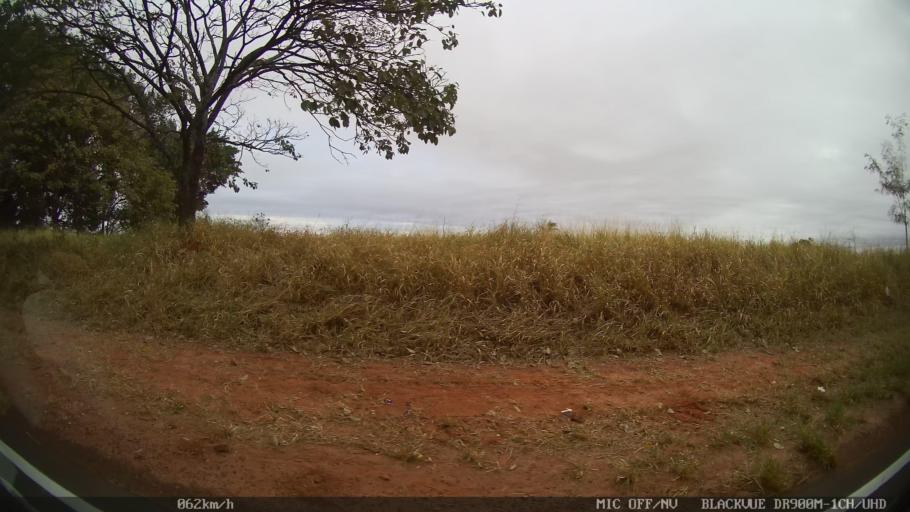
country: BR
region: Sao Paulo
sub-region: Sao Jose Do Rio Preto
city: Sao Jose do Rio Preto
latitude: -20.8276
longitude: -49.4245
